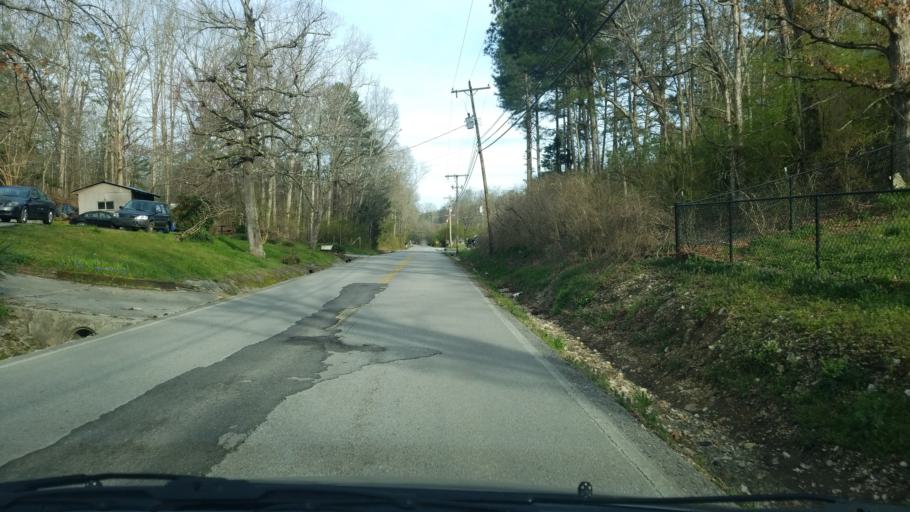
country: US
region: Tennessee
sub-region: Hamilton County
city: Harrison
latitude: 35.0605
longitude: -85.1101
